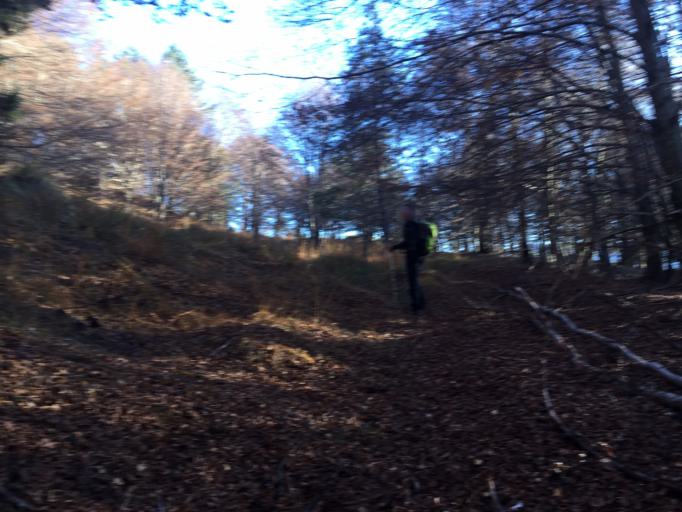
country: IT
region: Friuli Venezia Giulia
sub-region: Provincia di Udine
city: Chiusaforte
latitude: 46.4094
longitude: 13.2788
